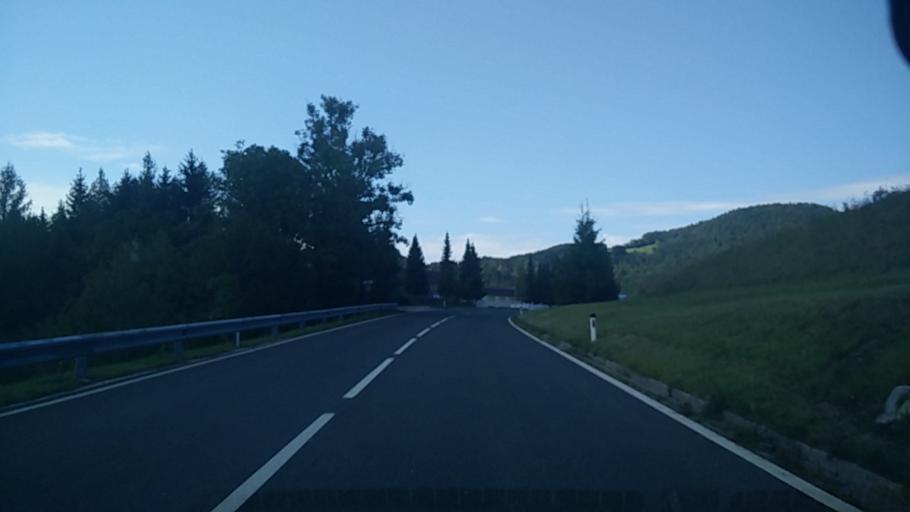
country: AT
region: Carinthia
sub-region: Politischer Bezirk Volkermarkt
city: Sittersdorf
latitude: 46.5393
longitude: 14.5980
